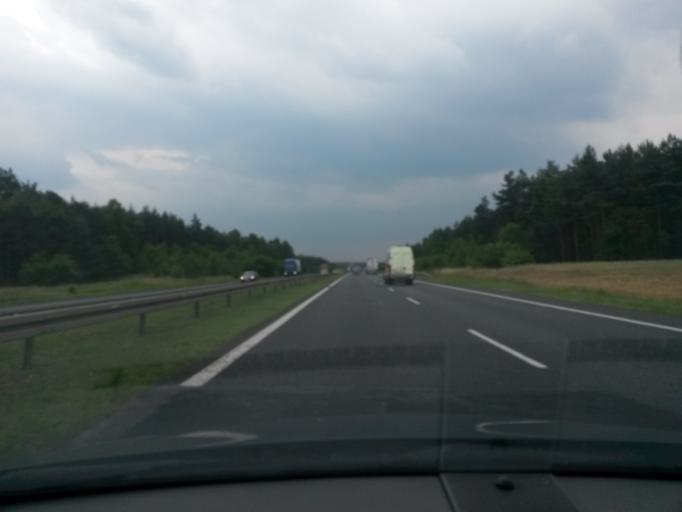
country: PL
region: Lodz Voivodeship
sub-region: Powiat radomszczanski
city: Radomsko
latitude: 51.0631
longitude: 19.3632
